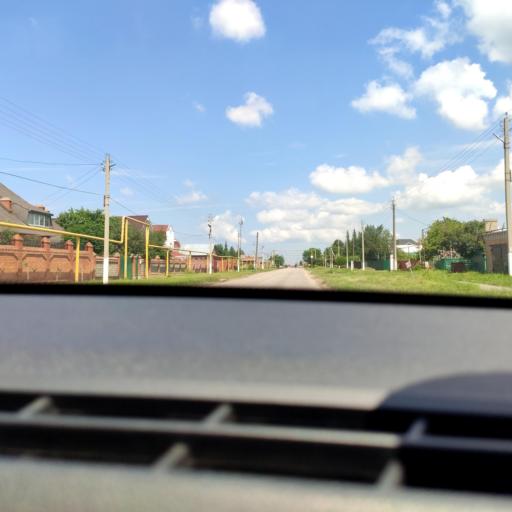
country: RU
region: Samara
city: Podstepki
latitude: 53.6183
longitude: 49.0461
